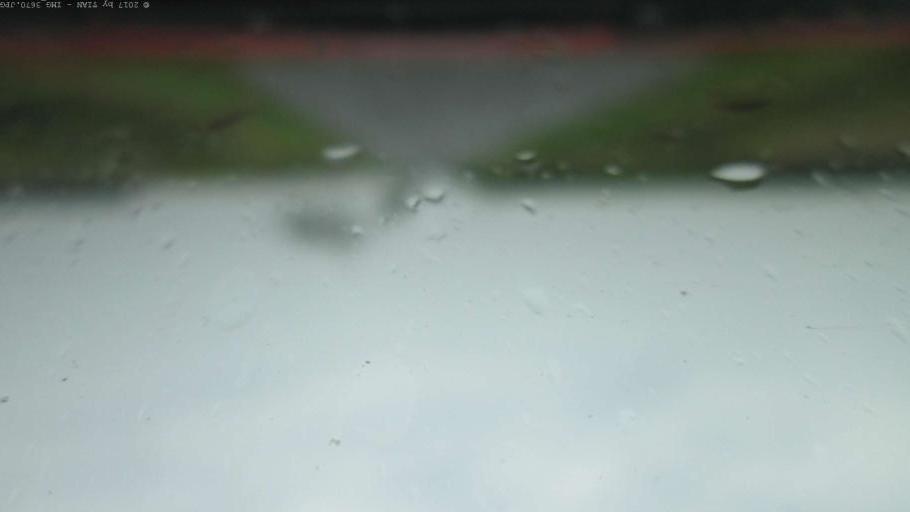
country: DE
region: Lower Saxony
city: Wolfsburg
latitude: 52.3433
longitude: 10.7674
